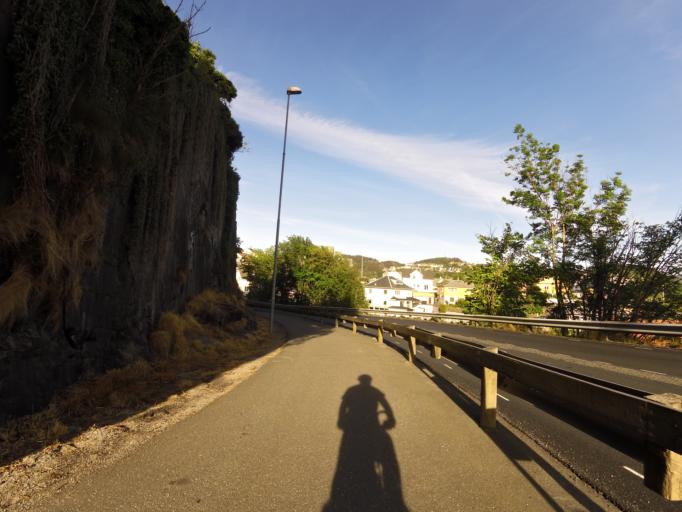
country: NO
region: Vest-Agder
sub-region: Flekkefjord
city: Flekkefjord
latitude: 58.2966
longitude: 6.6541
